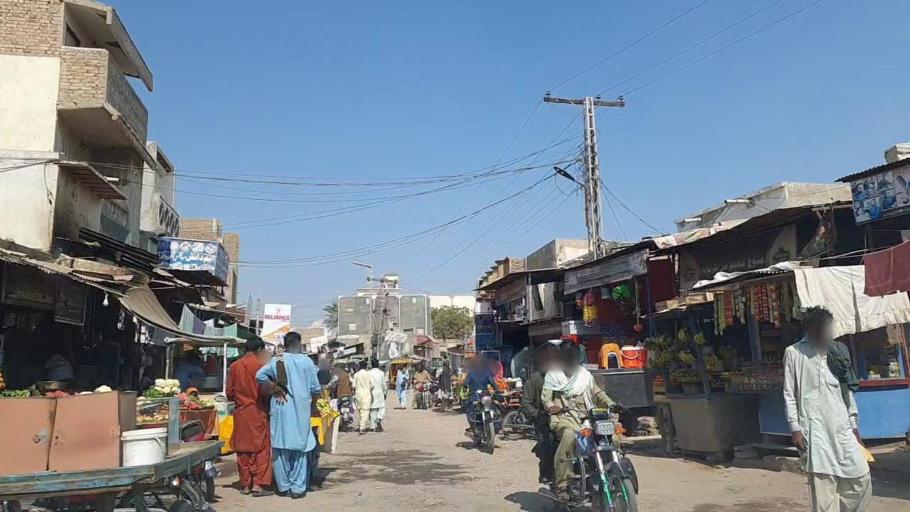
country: PK
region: Sindh
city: Naukot
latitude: 24.8552
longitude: 69.4026
